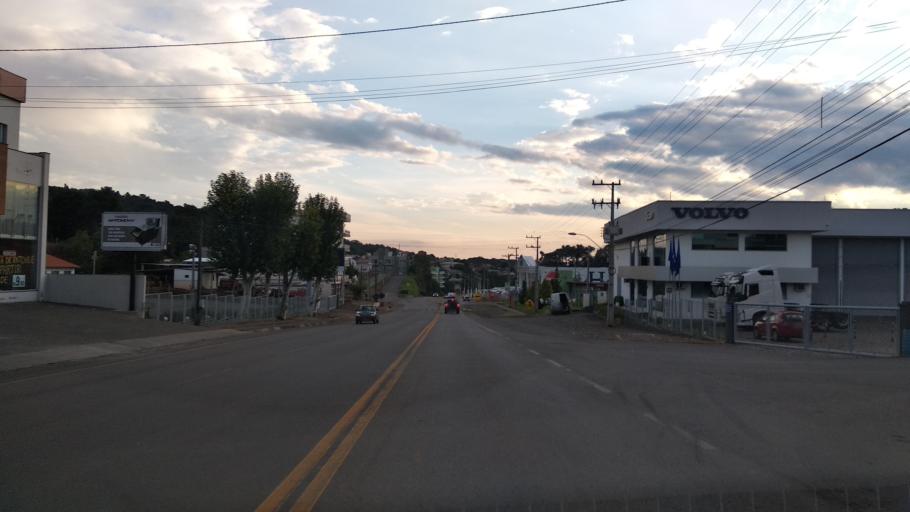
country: BR
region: Santa Catarina
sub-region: Videira
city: Videira
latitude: -26.9992
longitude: -51.1195
